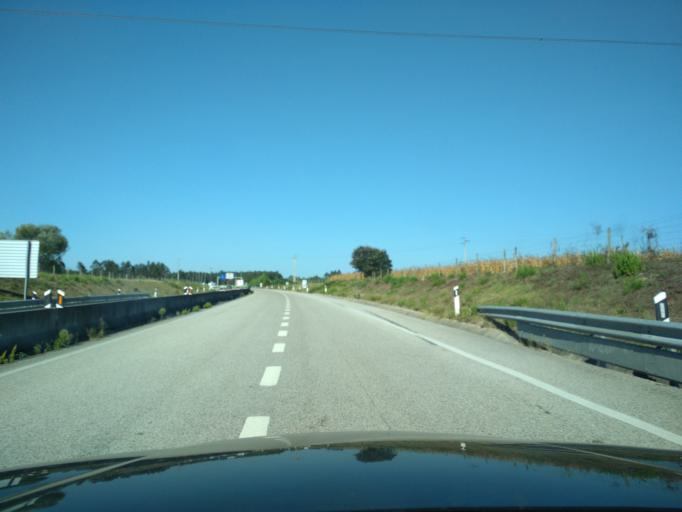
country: PT
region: Leiria
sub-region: Pombal
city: Lourical
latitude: 39.9890
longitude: -8.7808
